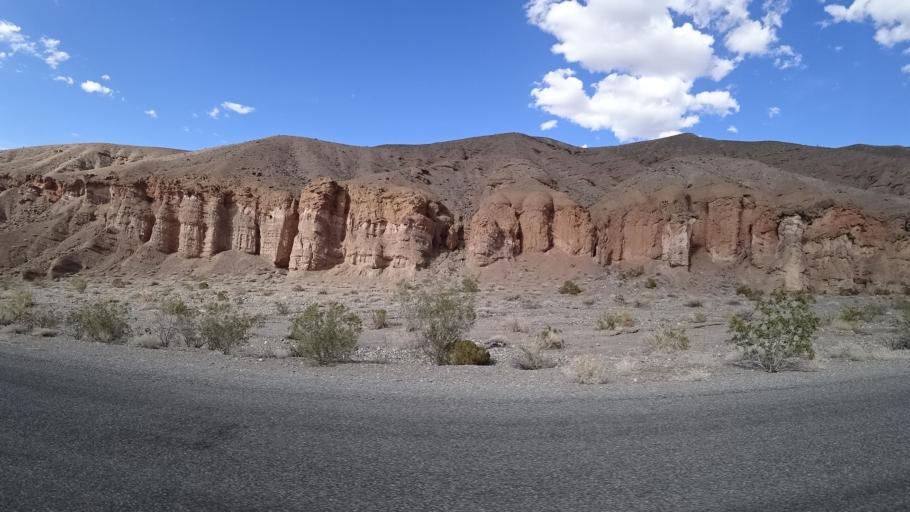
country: US
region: Nevada
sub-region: Nye County
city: Beatty
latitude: 36.4752
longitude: -117.2108
